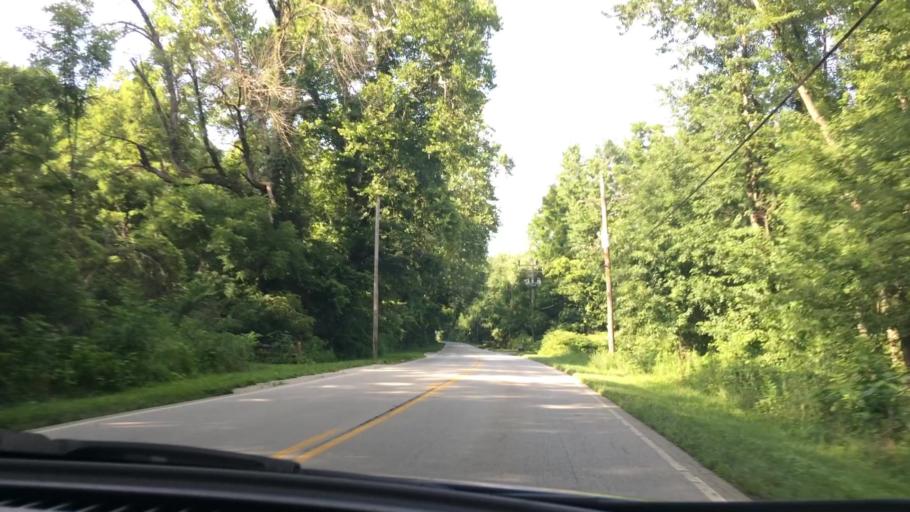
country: US
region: Indiana
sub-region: Tippecanoe County
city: West Lafayette
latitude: 40.4632
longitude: -86.8895
